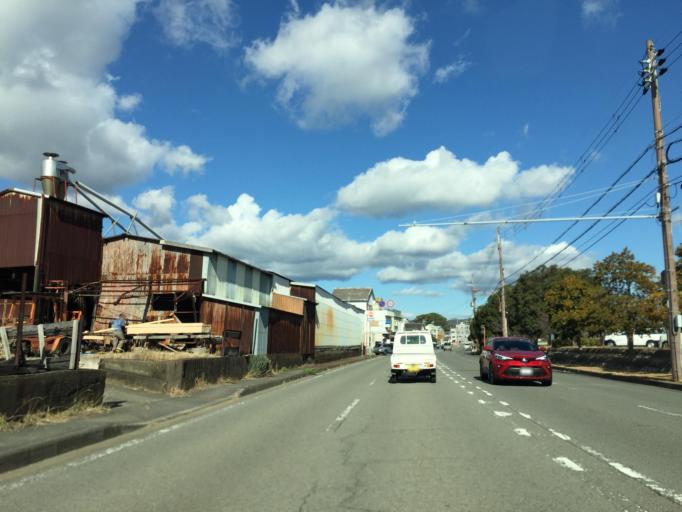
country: JP
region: Wakayama
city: Wakayama-shi
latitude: 34.2124
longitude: 135.1773
